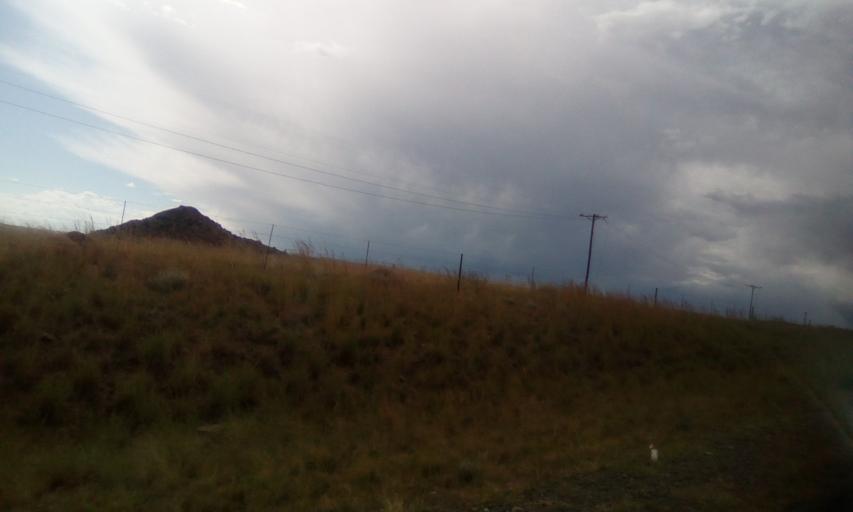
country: ZA
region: Orange Free State
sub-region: Thabo Mofutsanyana District Municipality
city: Ladybrand
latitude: -29.2586
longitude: 27.4335
